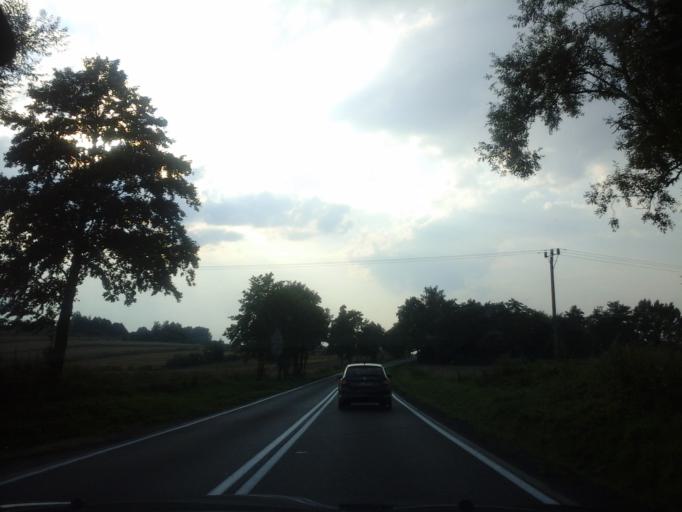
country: PL
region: Lesser Poland Voivodeship
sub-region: Powiat wadowicki
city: Spytkowice
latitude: 49.9865
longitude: 19.5290
